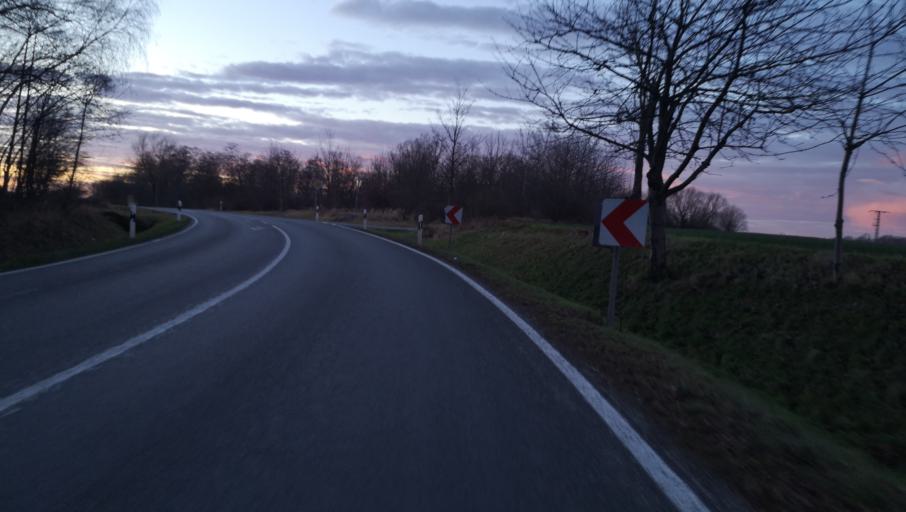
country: DE
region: Thuringia
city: Ronneburg
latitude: 50.8639
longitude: 12.1660
